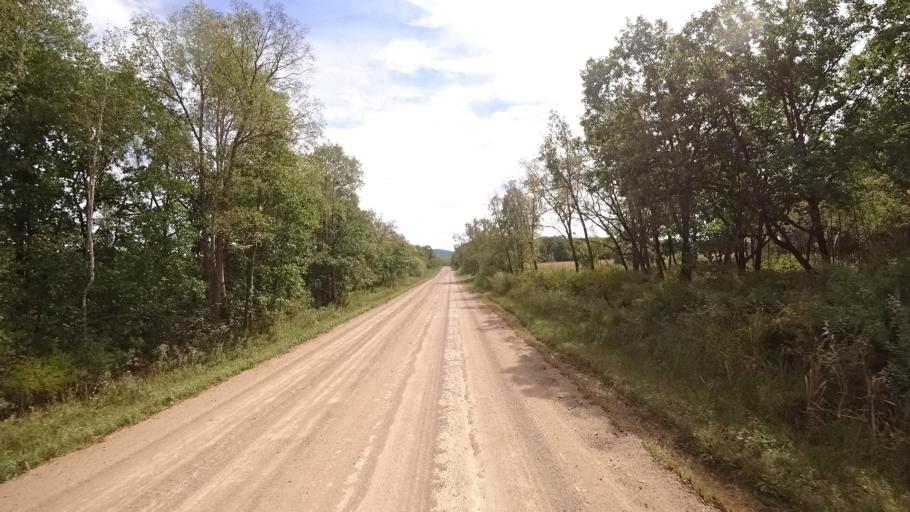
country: RU
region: Primorskiy
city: Yakovlevka
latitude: 44.6032
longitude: 133.6035
